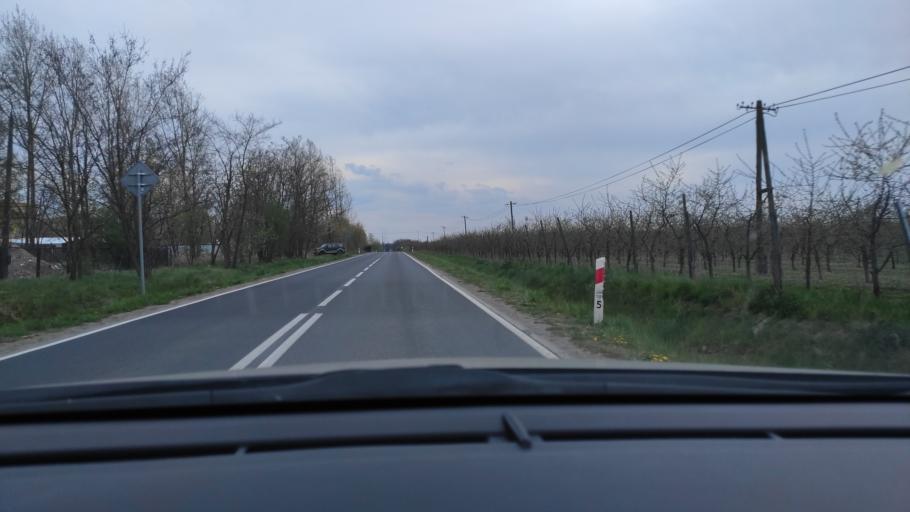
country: PL
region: Masovian Voivodeship
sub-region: Powiat zwolenski
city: Zwolen
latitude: 51.3644
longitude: 21.5644
